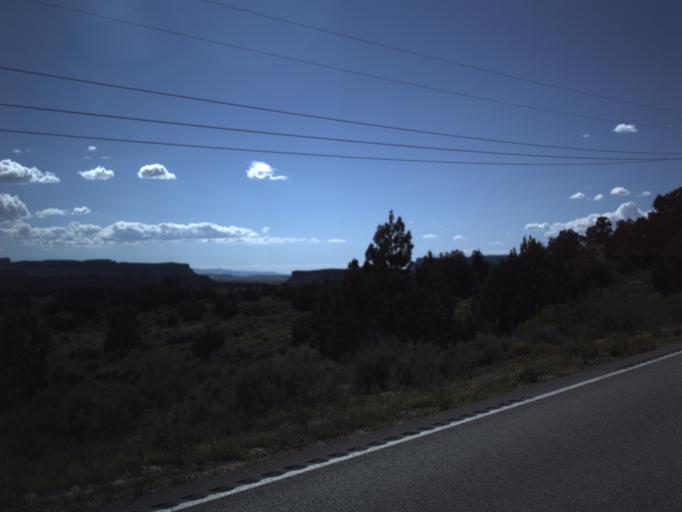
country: US
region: Arizona
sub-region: Mohave County
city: Colorado City
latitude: 37.0190
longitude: -113.0327
